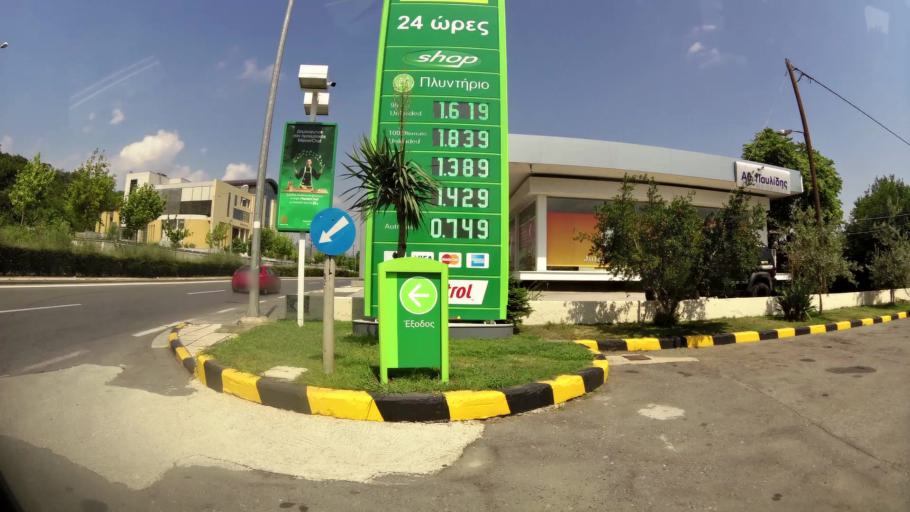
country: GR
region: Central Macedonia
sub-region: Nomos Imathias
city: Veroia
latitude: 40.5073
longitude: 22.2256
